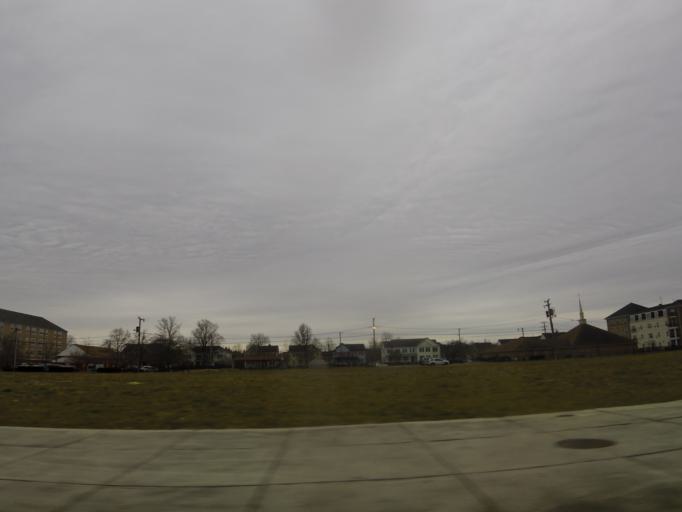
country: US
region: Virginia
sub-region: City of Portsmouth
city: Portsmouth
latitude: 36.8350
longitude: -76.3103
